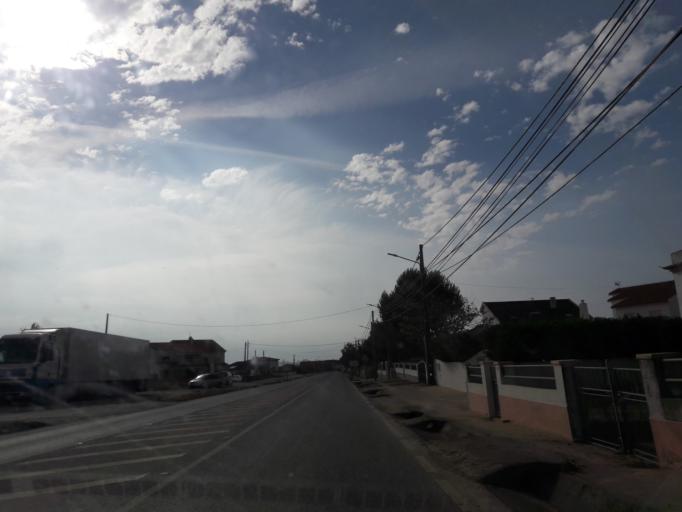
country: PT
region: Leiria
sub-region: Peniche
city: Atouguia da Baleia
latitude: 39.3420
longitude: -9.3337
